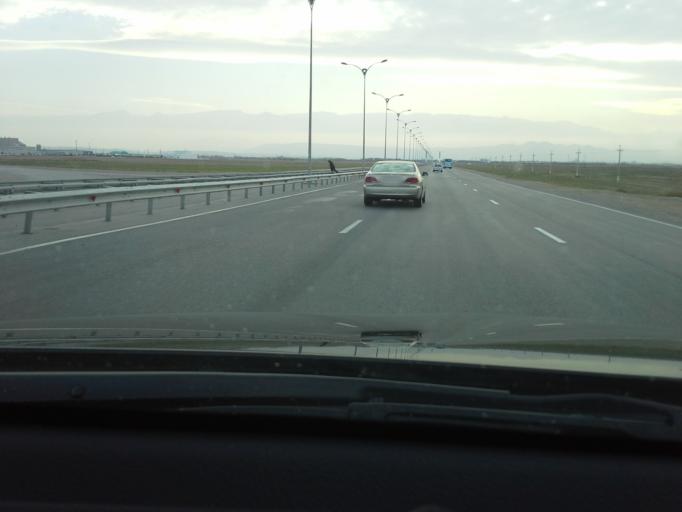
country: TM
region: Ahal
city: Abadan
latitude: 38.0609
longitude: 58.3075
